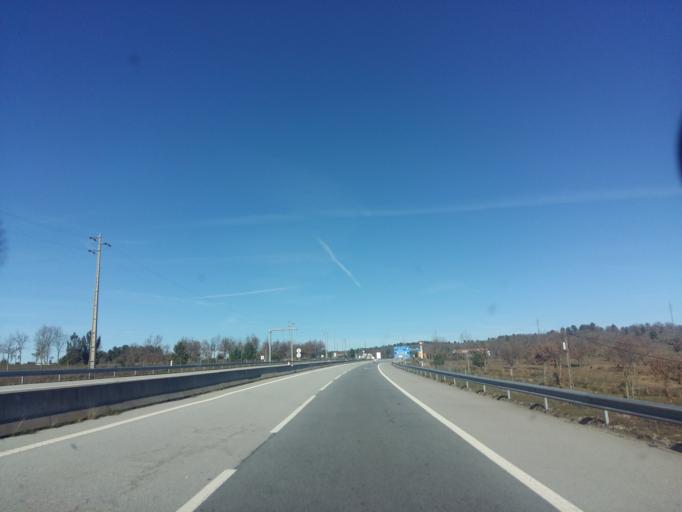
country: PT
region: Guarda
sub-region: Guarda
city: Sequeira
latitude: 40.5390
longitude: -7.2172
